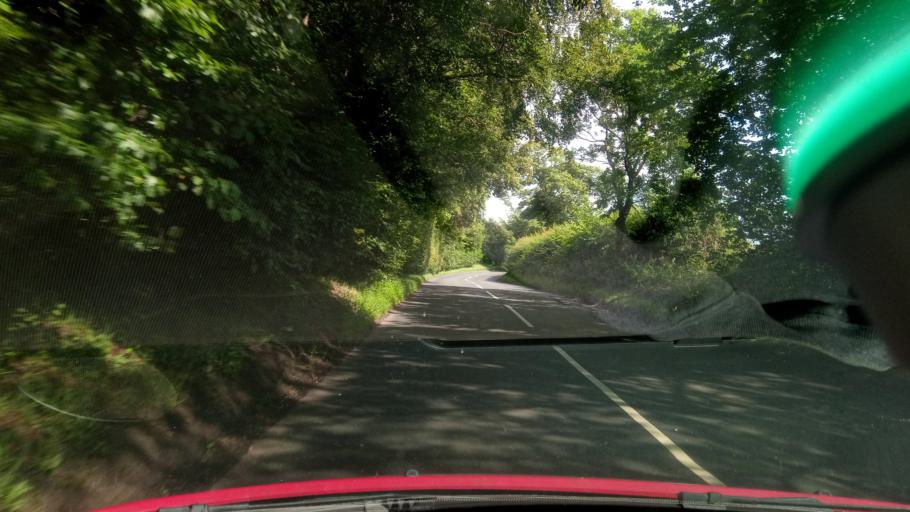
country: GB
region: Scotland
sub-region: East Lothian
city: Ormiston
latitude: 55.8962
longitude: -2.9449
